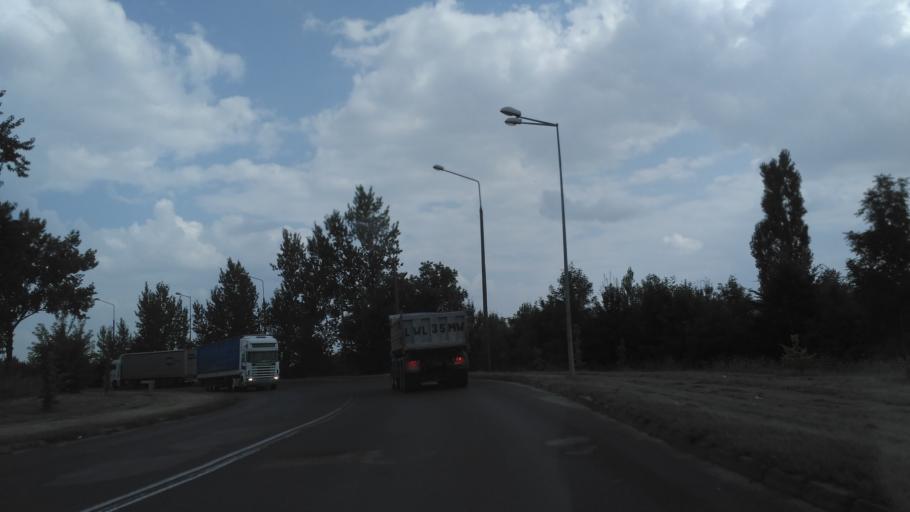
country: PL
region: Lublin Voivodeship
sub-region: Chelm
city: Chelm
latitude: 51.1429
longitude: 23.4840
